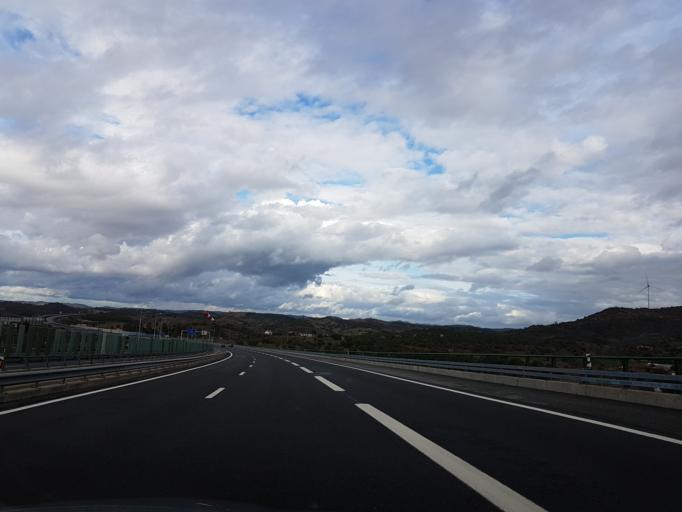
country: PT
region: Faro
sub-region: Silves
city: Sao Bartolomeu de Messines
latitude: 37.2493
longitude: -8.2553
